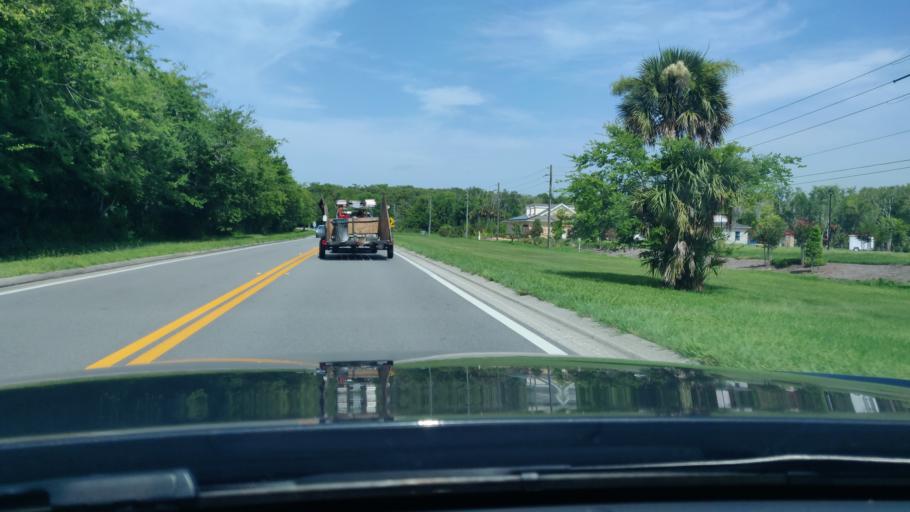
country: US
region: Florida
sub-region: Flagler County
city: Palm Coast
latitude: 29.5534
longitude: -81.1820
